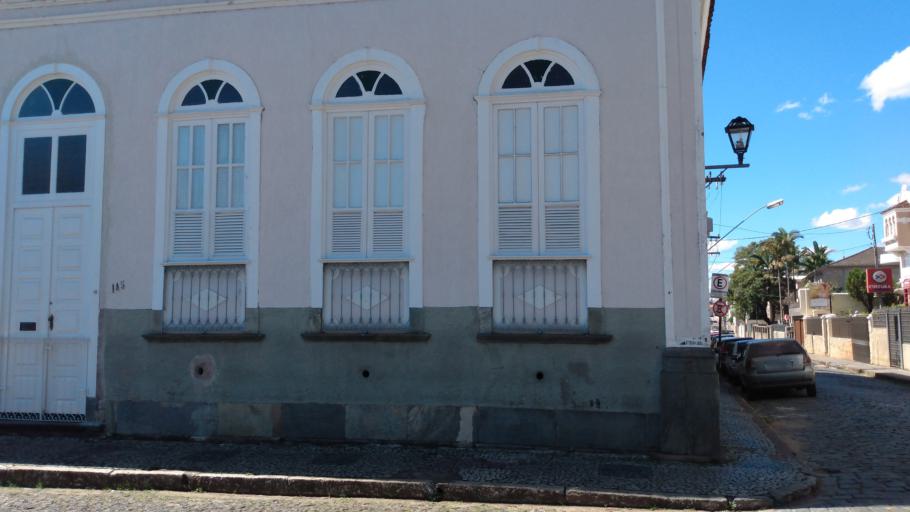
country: BR
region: Minas Gerais
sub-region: Sao Joao Del Rei
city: Sao Joao del Rei
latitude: -21.1381
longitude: -44.2606
